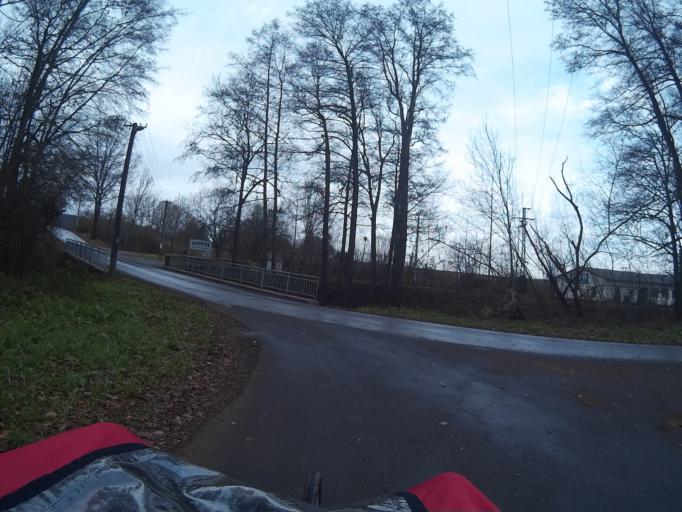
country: CZ
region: Plzensky
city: St'ahlavy
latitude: 49.6733
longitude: 13.4963
